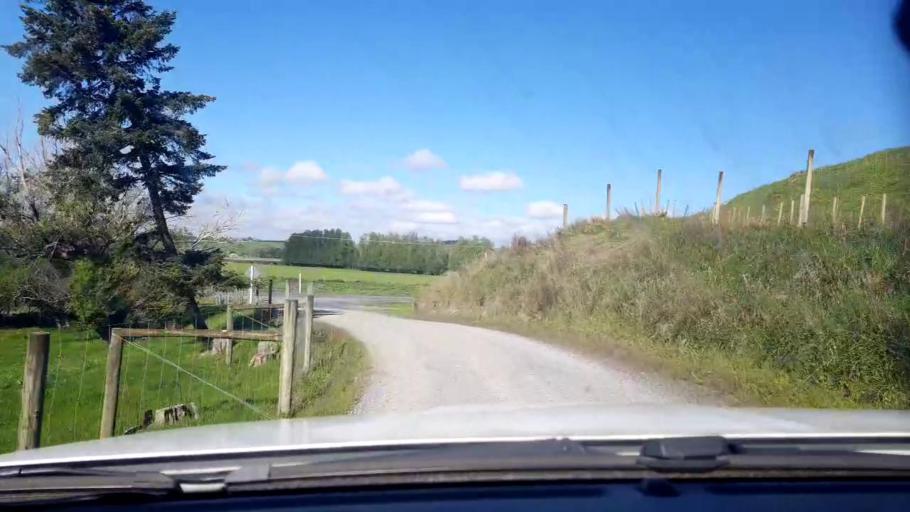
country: NZ
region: Otago
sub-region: Clutha District
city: Balclutha
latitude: -46.2233
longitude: 169.7327
